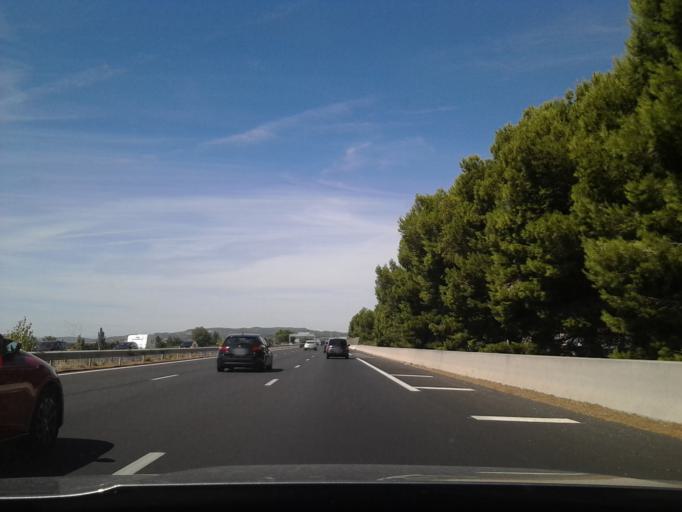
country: FR
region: Languedoc-Roussillon
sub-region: Departement de l'Aude
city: Narbonne
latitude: 43.1703
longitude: 3.0141
